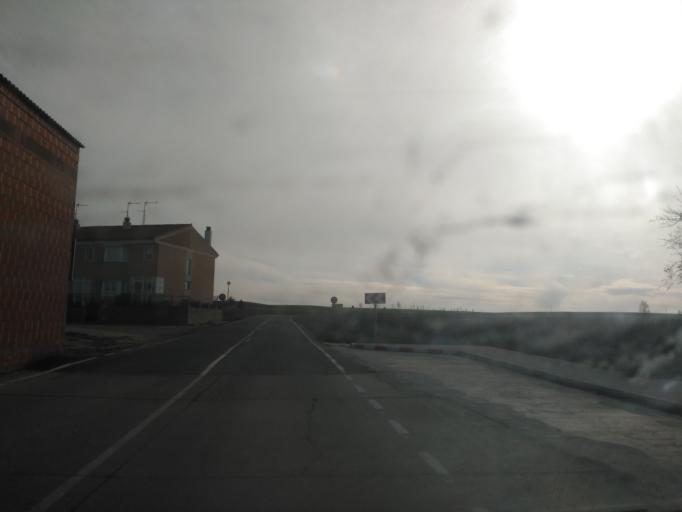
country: ES
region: Castille and Leon
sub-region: Provincia de Salamanca
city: Moriscos
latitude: 41.0070
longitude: -5.5836
